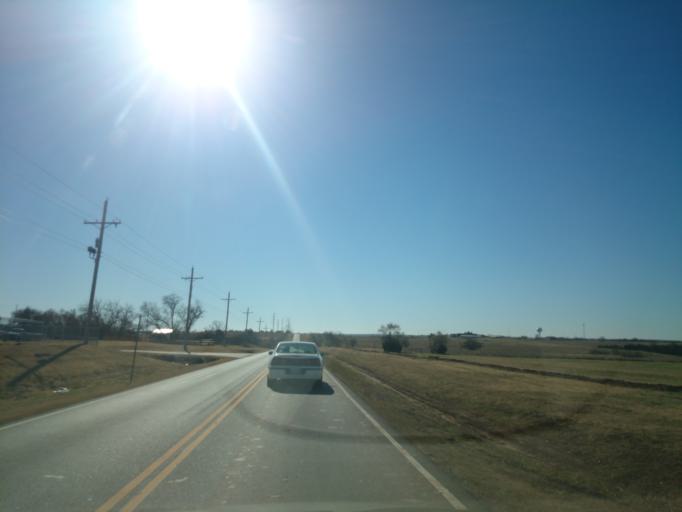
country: US
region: Oklahoma
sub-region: Payne County
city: Stillwater
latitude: 36.1443
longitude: -97.0875
